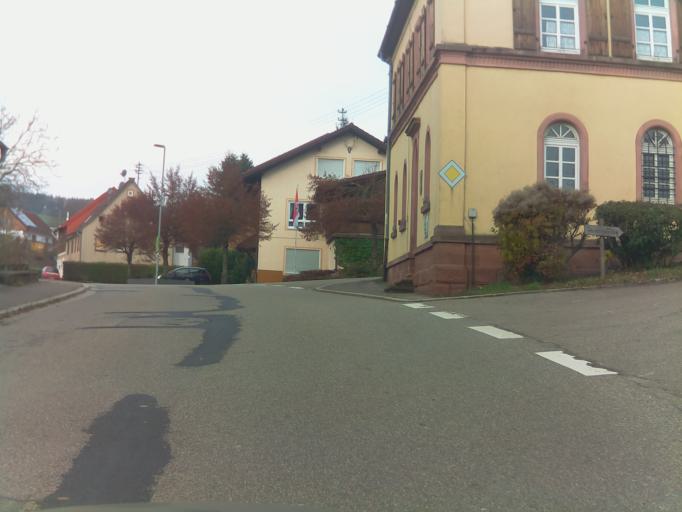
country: DE
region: Baden-Wuerttemberg
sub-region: Karlsruhe Region
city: Reichartshausen
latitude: 49.3952
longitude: 8.9291
